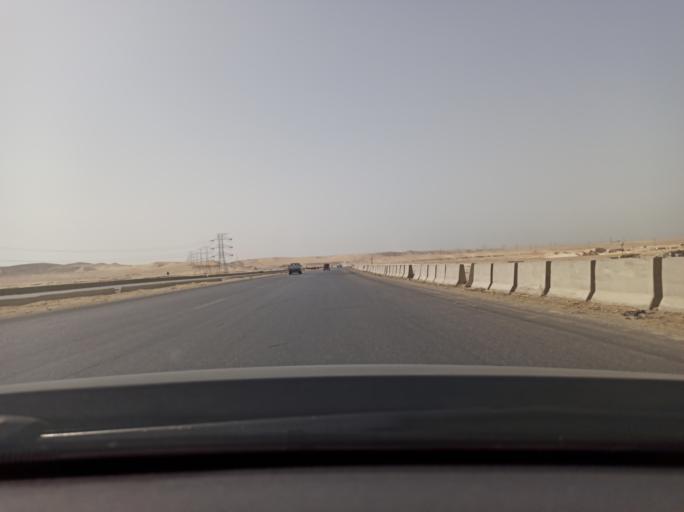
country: EG
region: Al Jizah
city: As Saff
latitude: 29.5284
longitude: 31.3858
